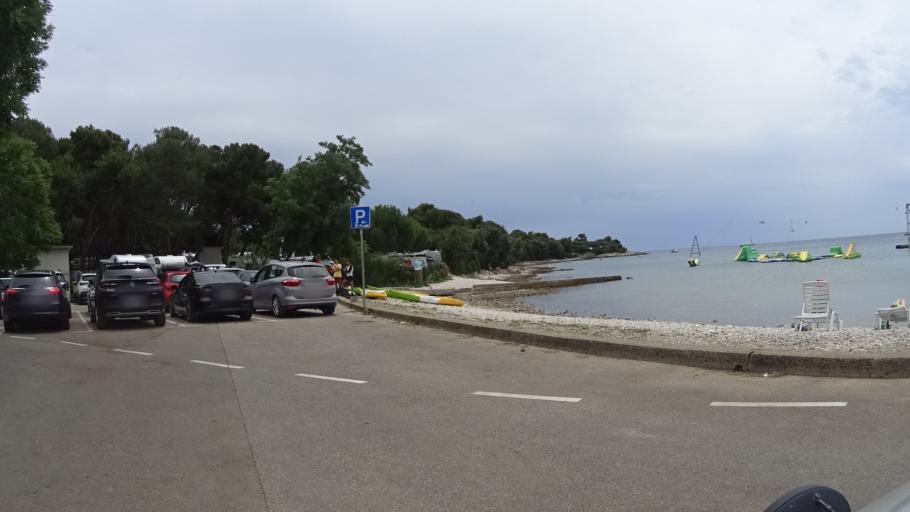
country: HR
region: Istarska
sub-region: Grad Pula
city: Pula
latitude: 44.8600
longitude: 13.8143
